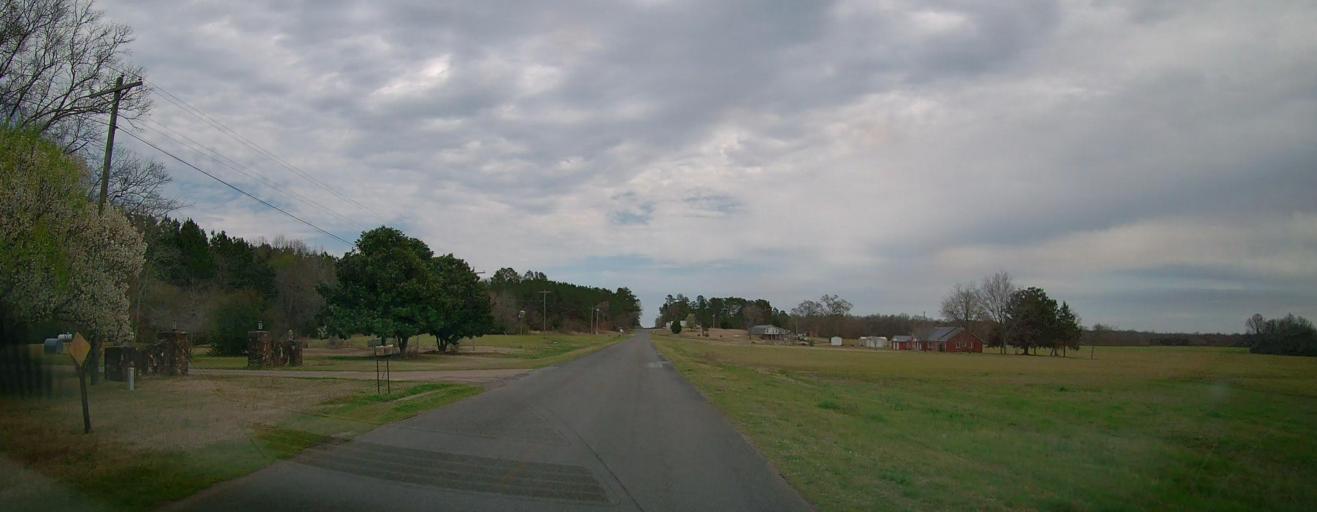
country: US
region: Alabama
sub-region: Marion County
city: Hamilton
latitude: 34.1913
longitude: -88.1509
